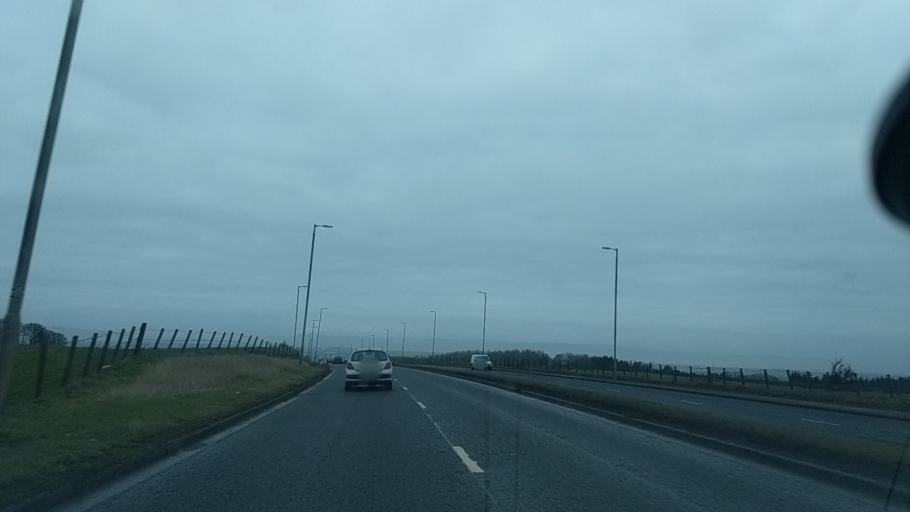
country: GB
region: Scotland
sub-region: South Lanarkshire
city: East Kilbride
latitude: 55.7932
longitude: -4.1671
